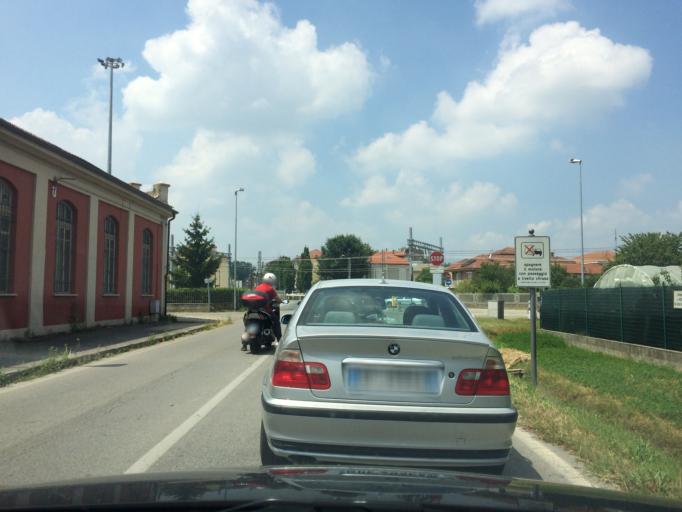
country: IT
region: Piedmont
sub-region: Provincia di Cuneo
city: Racconigi
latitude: 44.7723
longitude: 7.6873
